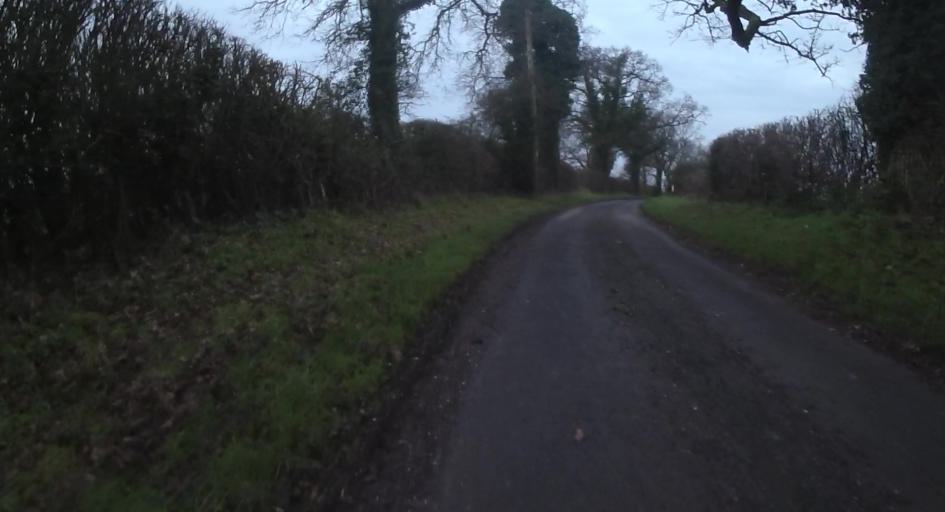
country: GB
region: England
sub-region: Hampshire
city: Overton
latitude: 51.2624
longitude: -1.3106
